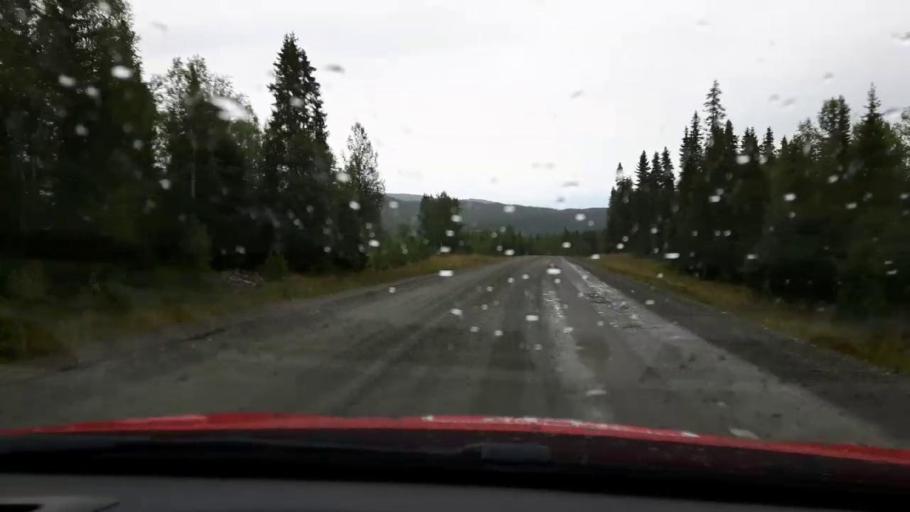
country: SE
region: Jaemtland
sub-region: Are Kommun
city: Are
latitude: 63.4118
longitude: 12.7819
